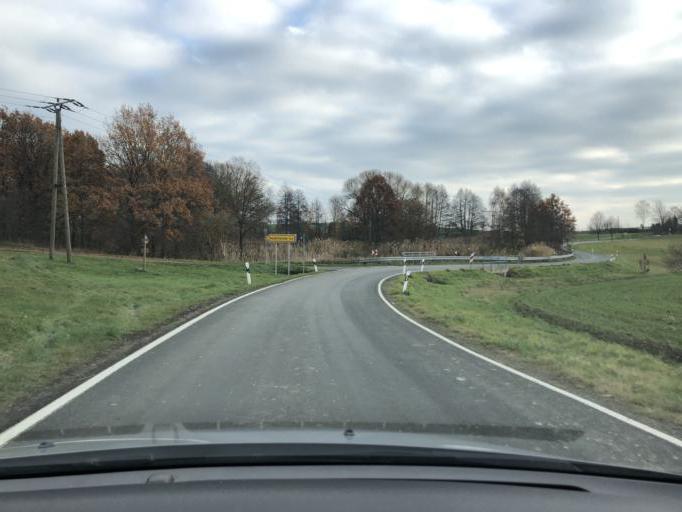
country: DE
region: Saxony
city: Mutzschen
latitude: 51.2804
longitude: 12.8763
